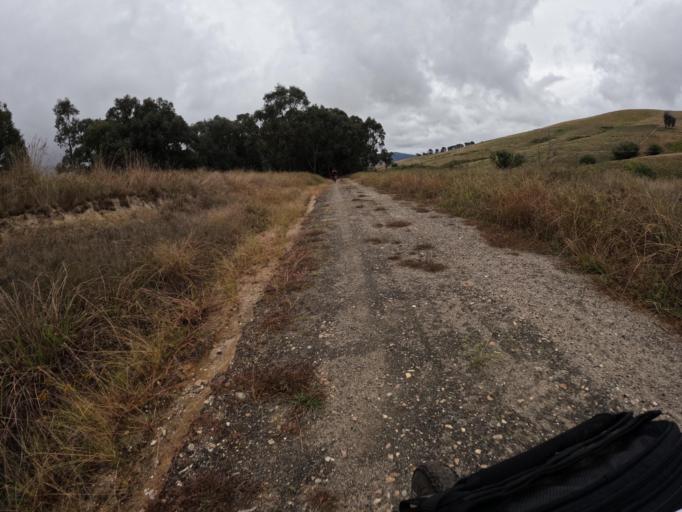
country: AU
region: New South Wales
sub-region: Greater Hume Shire
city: Holbrook
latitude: -36.1612
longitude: 147.4087
